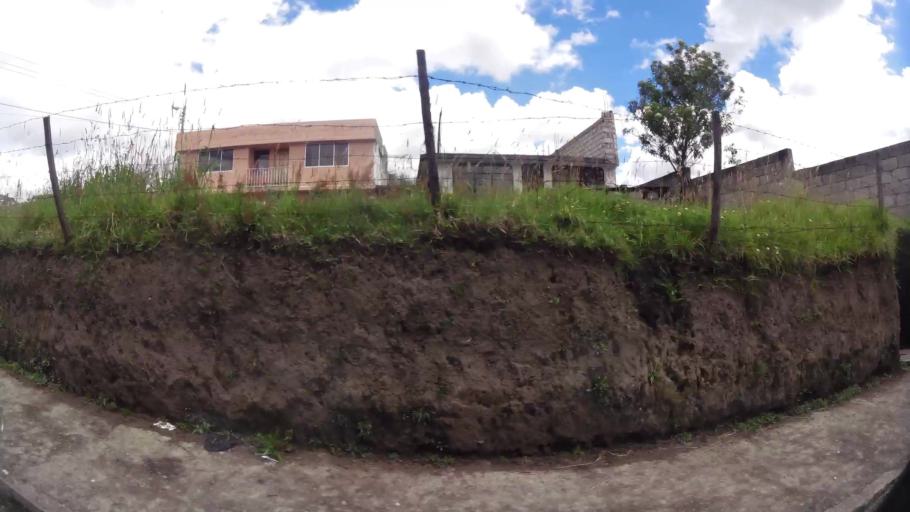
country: EC
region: Pichincha
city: Sangolqui
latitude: -0.3413
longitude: -78.5693
